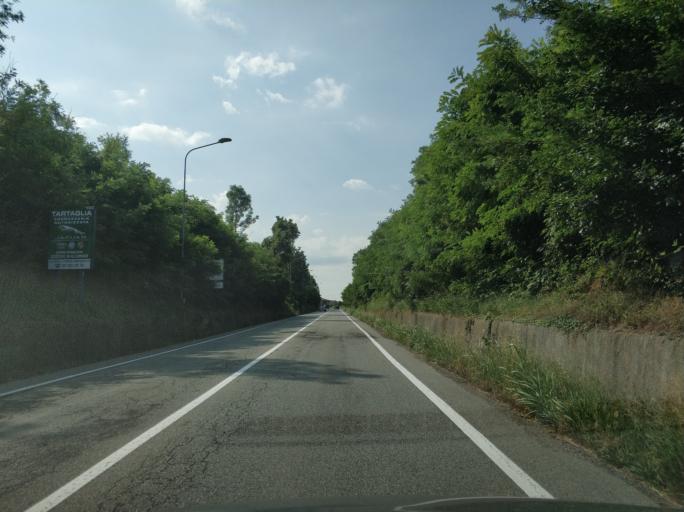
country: IT
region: Piedmont
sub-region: Provincia di Torino
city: Poirino
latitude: 44.9195
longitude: 7.8388
